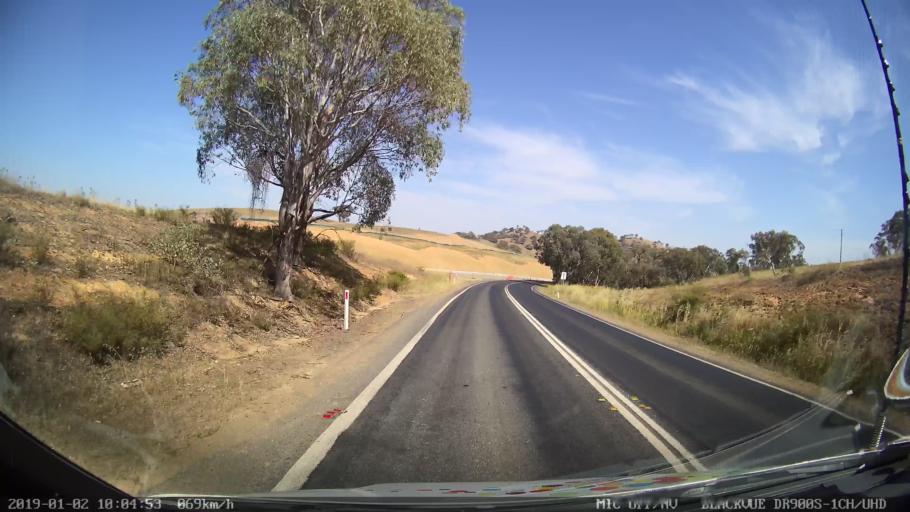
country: AU
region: New South Wales
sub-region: Gundagai
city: Gundagai
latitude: -35.1639
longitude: 148.1203
